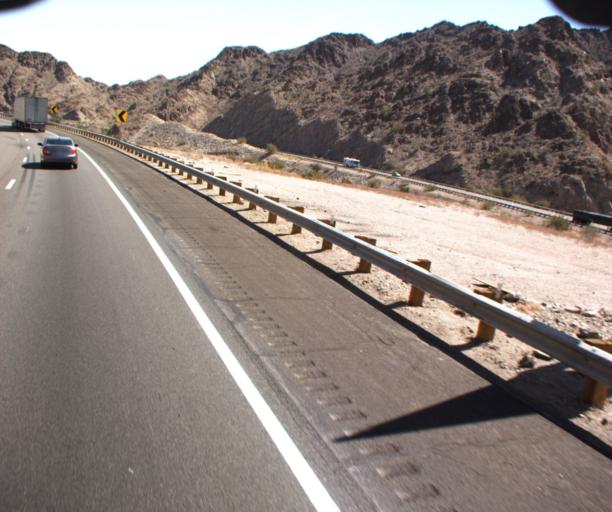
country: US
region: Arizona
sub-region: Yuma County
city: Fortuna Foothills
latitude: 32.6604
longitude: -114.3242
